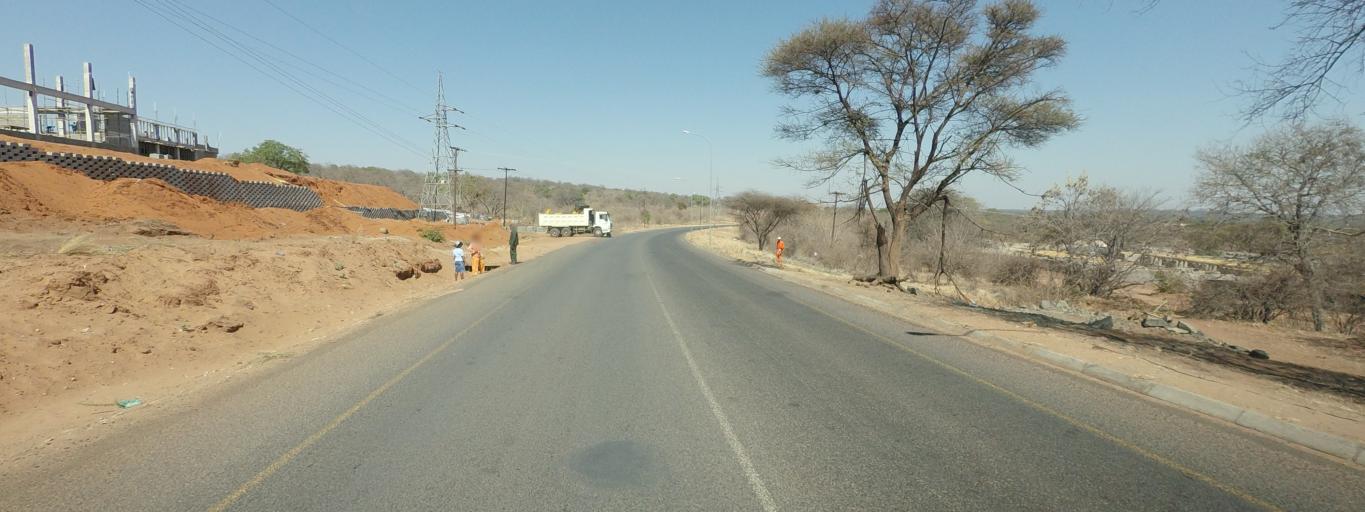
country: BW
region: North West
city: Kasane
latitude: -17.7998
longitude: 25.2247
